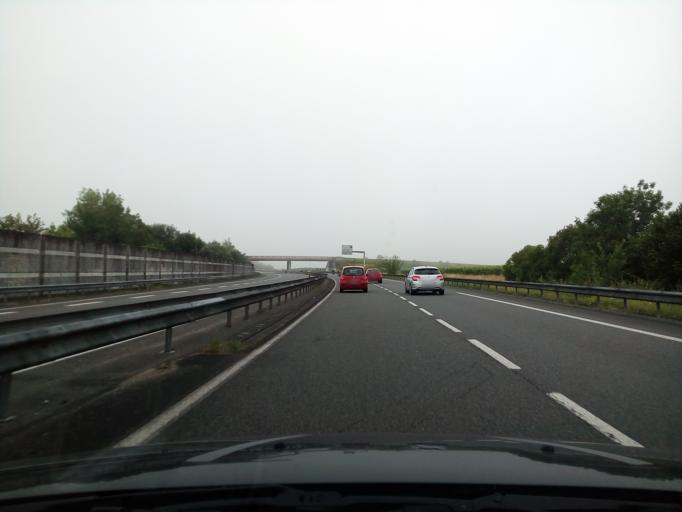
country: FR
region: Poitou-Charentes
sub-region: Departement de la Charente
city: Jarnac
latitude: 45.6947
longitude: -0.1346
